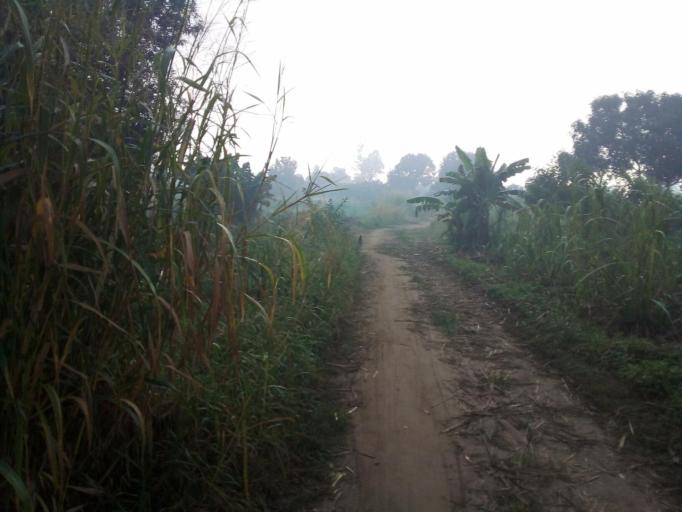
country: MZ
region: Zambezia
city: Quelimane
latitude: -17.5871
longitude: 36.6858
